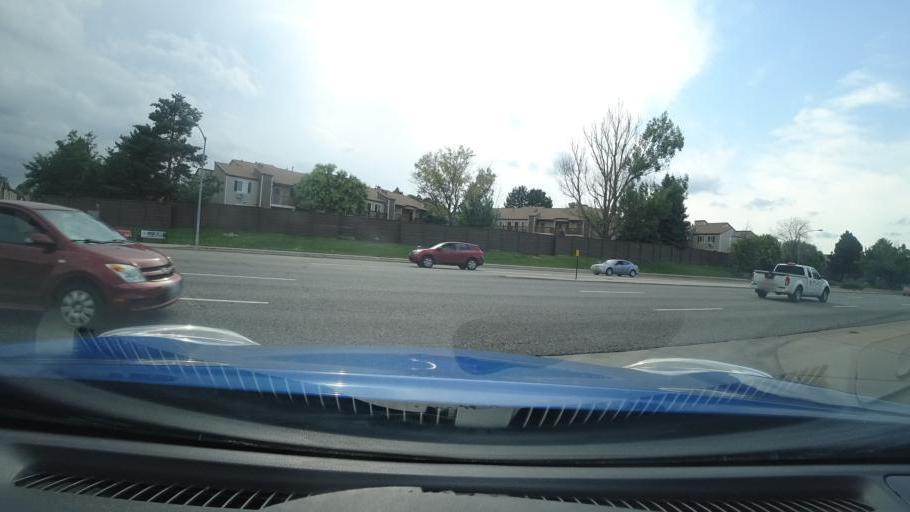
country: US
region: Colorado
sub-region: Adams County
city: Aurora
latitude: 39.6929
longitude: -104.8096
